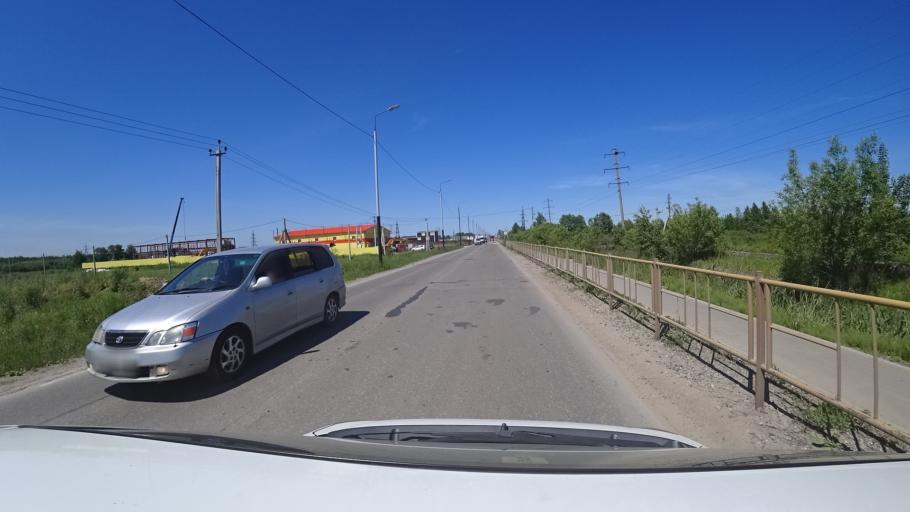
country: RU
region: Khabarovsk Krai
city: Topolevo
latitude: 48.4855
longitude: 135.1828
